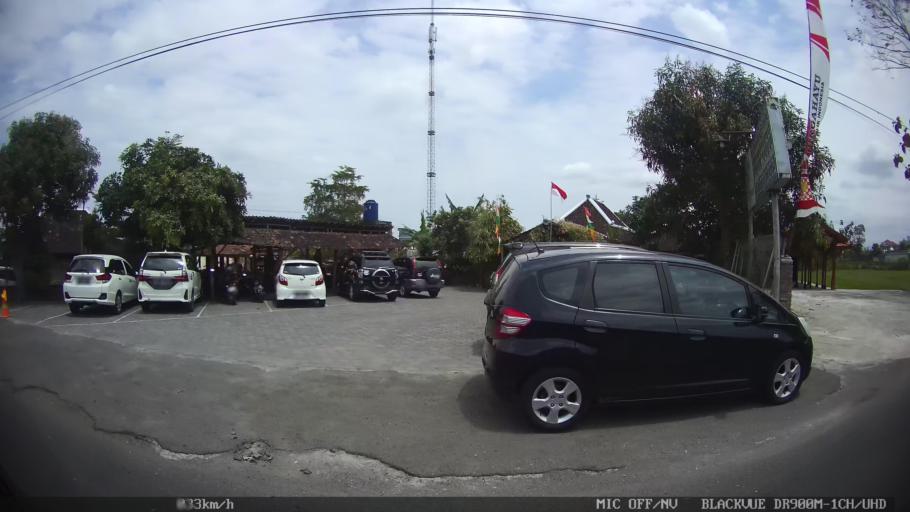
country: ID
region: Central Java
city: Candi Prambanan
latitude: -7.7876
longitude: 110.4813
